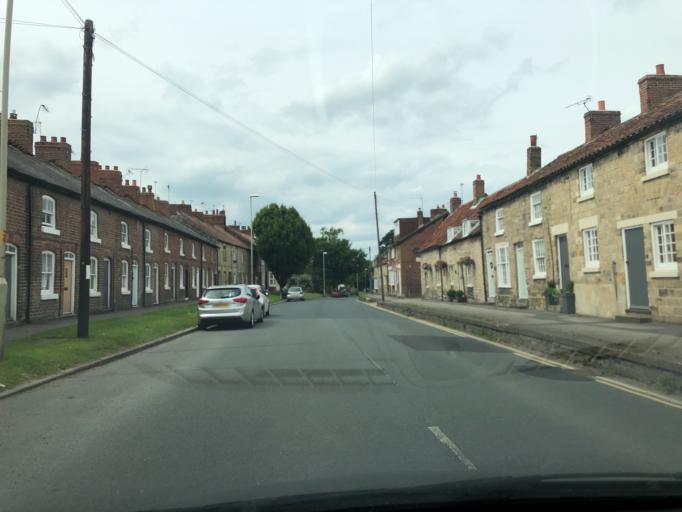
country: GB
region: England
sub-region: North Yorkshire
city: Pickering
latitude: 54.2471
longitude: -0.7881
